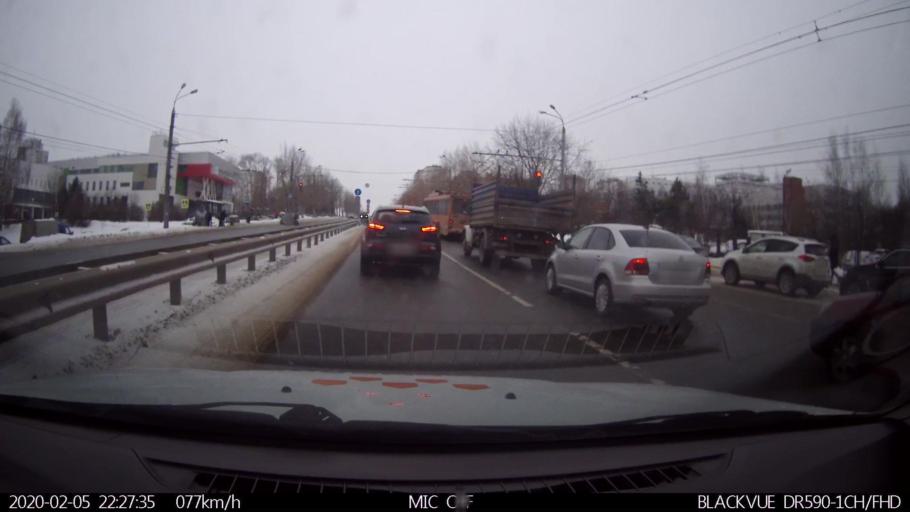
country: RU
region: Nizjnij Novgorod
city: Imeni Stepana Razina
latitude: 54.7609
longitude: 44.1179
